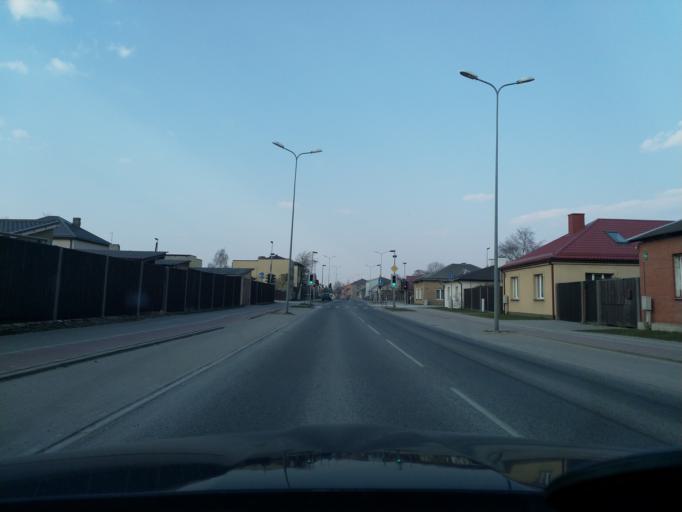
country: LV
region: Liepaja
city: Liepaja
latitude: 56.5015
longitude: 21.0222
